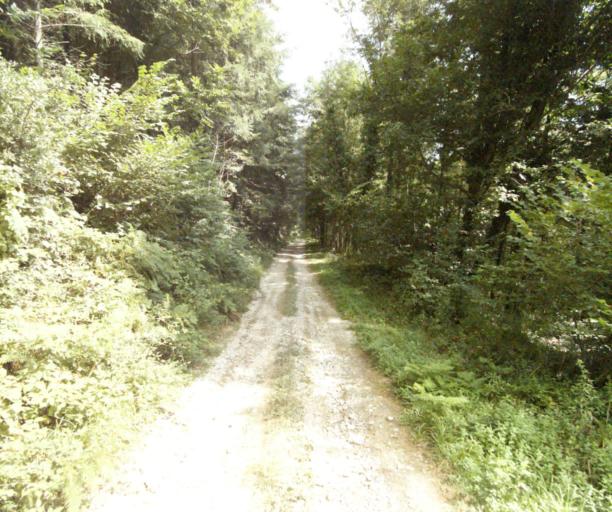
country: FR
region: Midi-Pyrenees
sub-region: Departement du Tarn
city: Soreze
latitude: 43.4545
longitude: 2.1060
